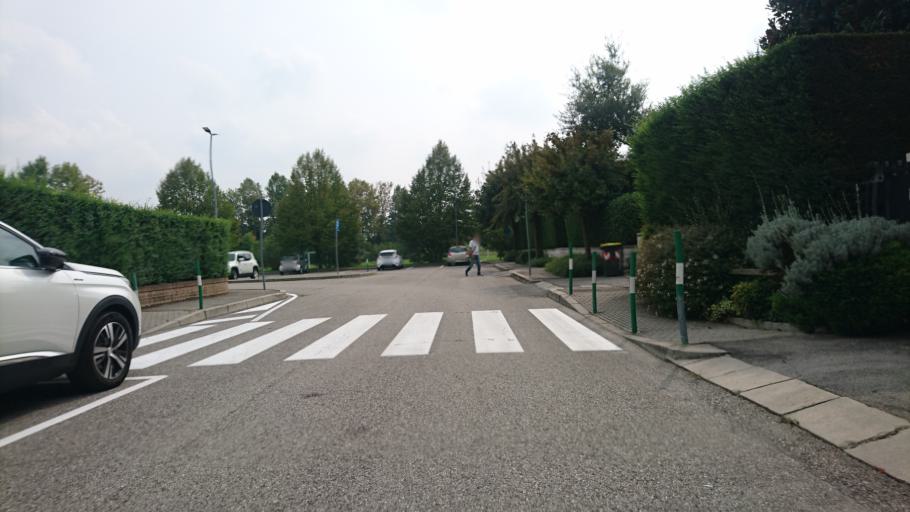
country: IT
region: Veneto
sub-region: Provincia di Padova
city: Tencarola
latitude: 45.3894
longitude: 11.8171
